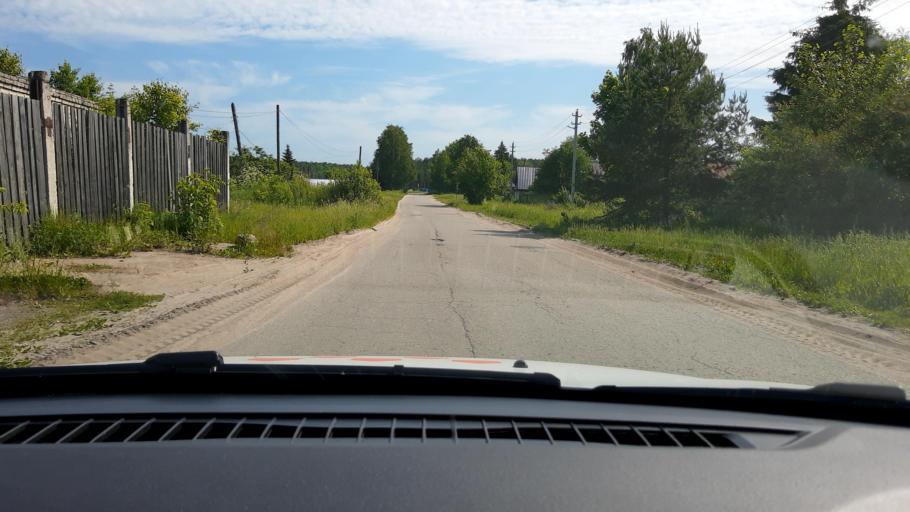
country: RU
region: Nizjnij Novgorod
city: Linda
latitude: 56.6829
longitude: 44.1982
